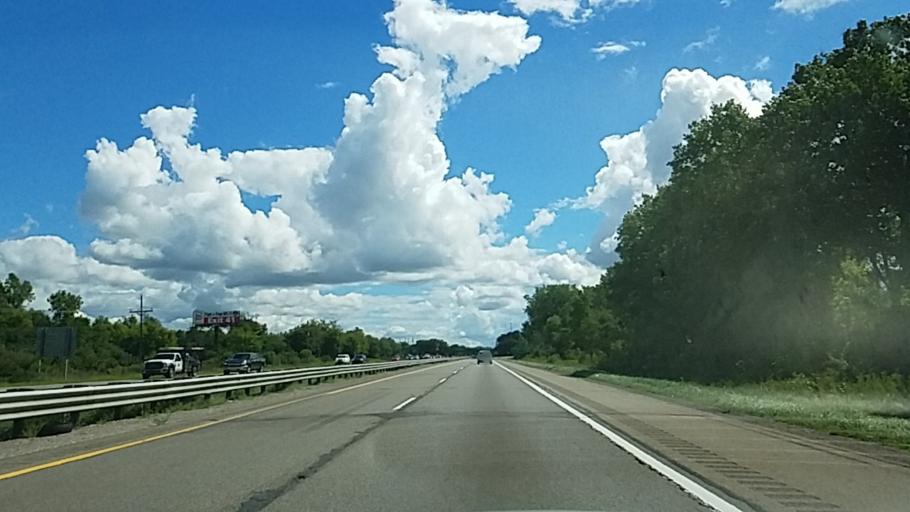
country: US
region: Michigan
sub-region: Livingston County
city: Whitmore Lake
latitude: 42.3846
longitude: -83.7602
